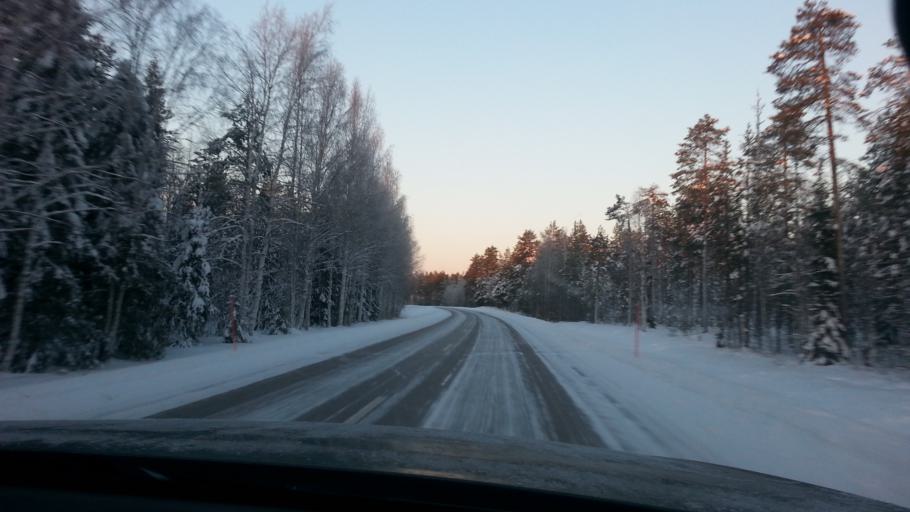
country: FI
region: Lapland
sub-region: Rovaniemi
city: Rovaniemi
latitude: 66.7725
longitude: 25.4598
